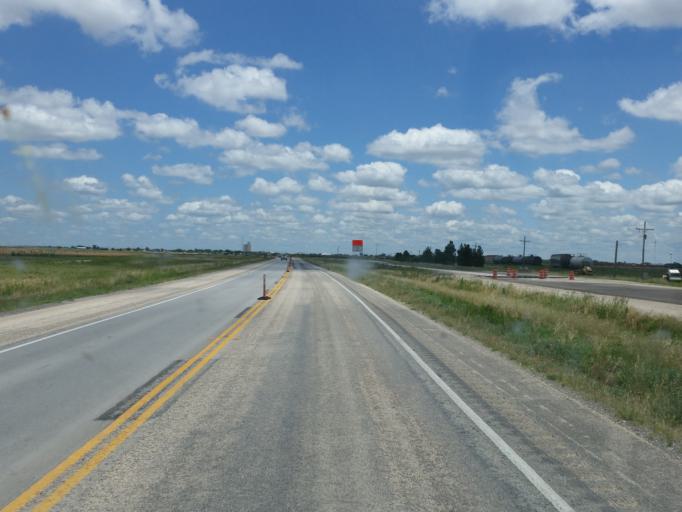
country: US
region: Texas
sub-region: Nolan County
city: Roscoe
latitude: 32.4550
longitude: -100.5598
